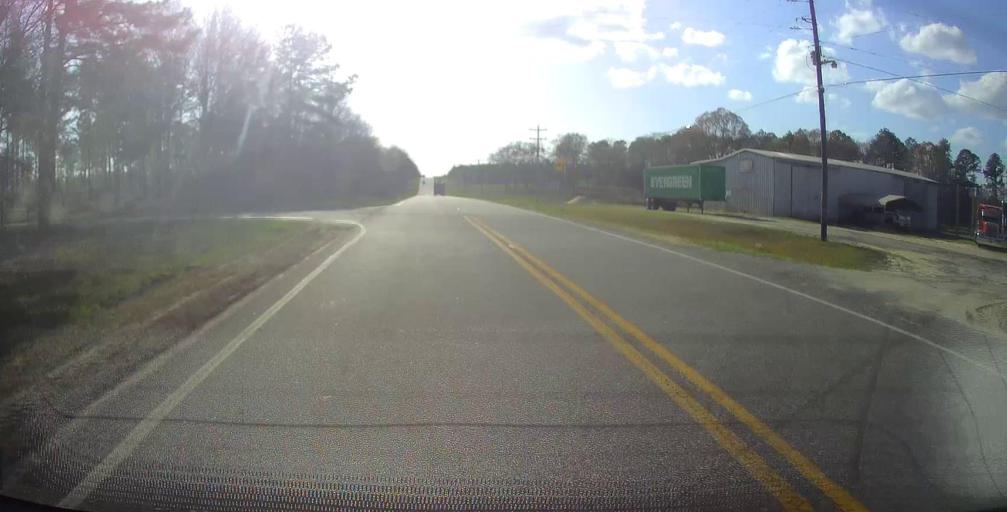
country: US
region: Georgia
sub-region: Montgomery County
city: Mount Vernon
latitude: 32.1729
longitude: -82.6832
